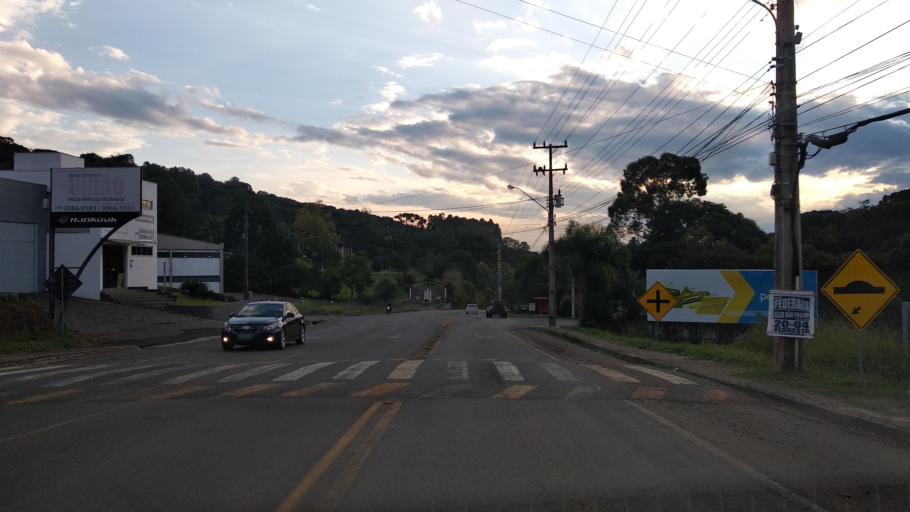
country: BR
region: Santa Catarina
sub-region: Videira
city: Videira
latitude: -27.0019
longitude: -51.1271
